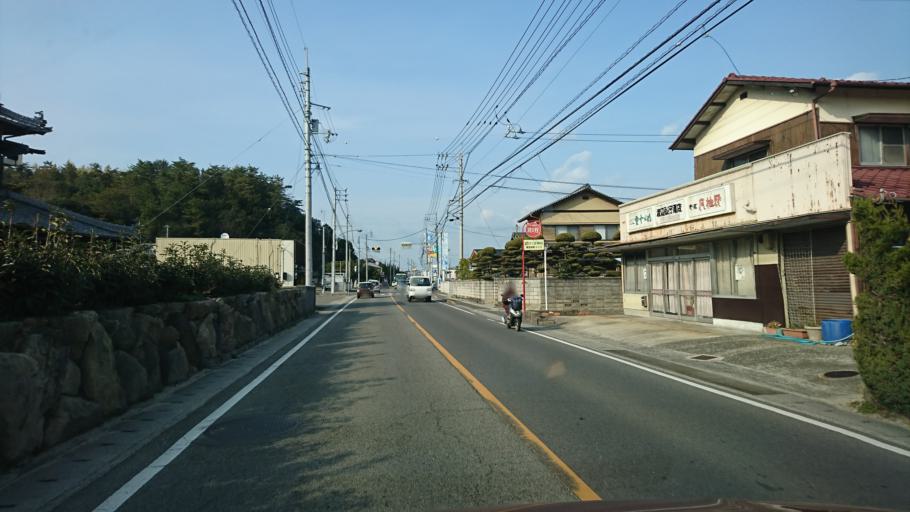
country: JP
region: Ehime
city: Saijo
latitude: 34.0289
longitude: 133.0371
